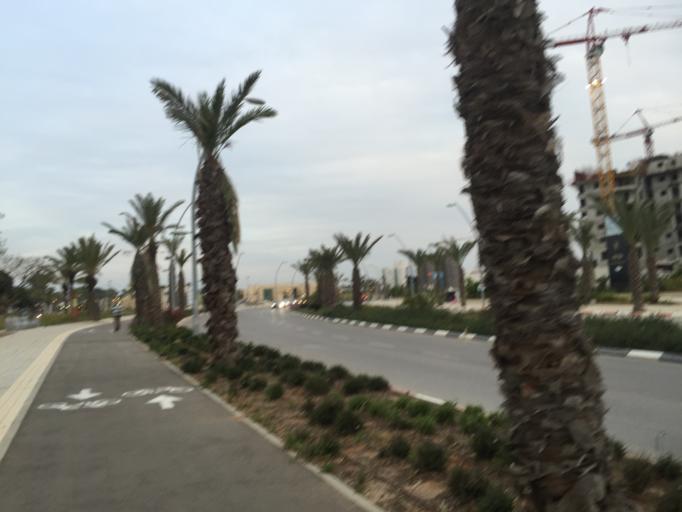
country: IL
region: Haifa
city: Qesarya
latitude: 32.5053
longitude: 34.9170
